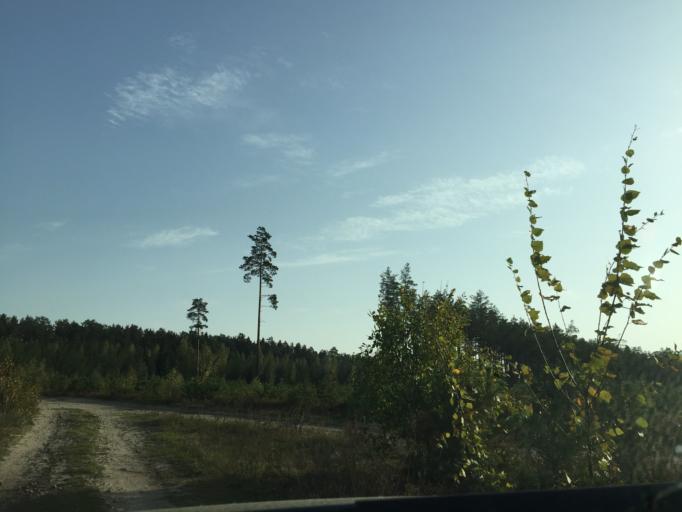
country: LV
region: Garkalne
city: Garkalne
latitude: 56.9680
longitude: 24.4211
